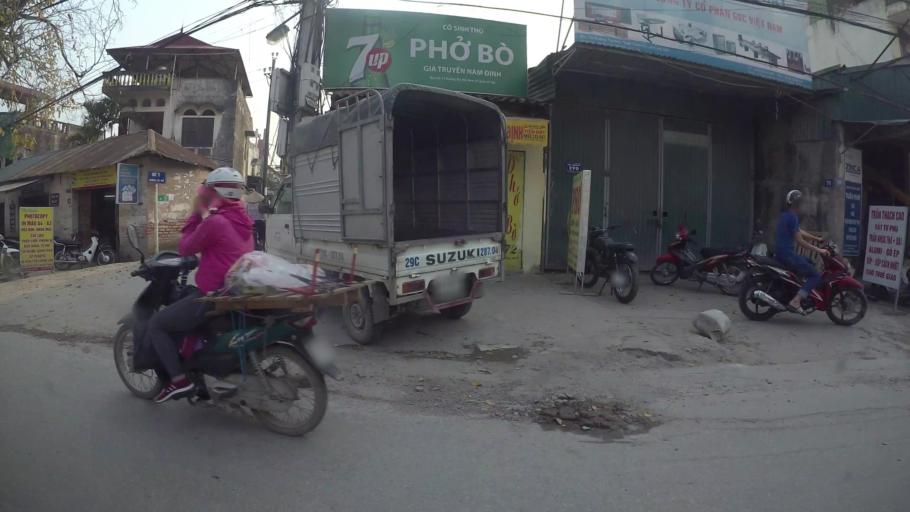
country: VN
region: Ha Noi
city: Cau Dien
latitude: 21.0040
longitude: 105.7497
